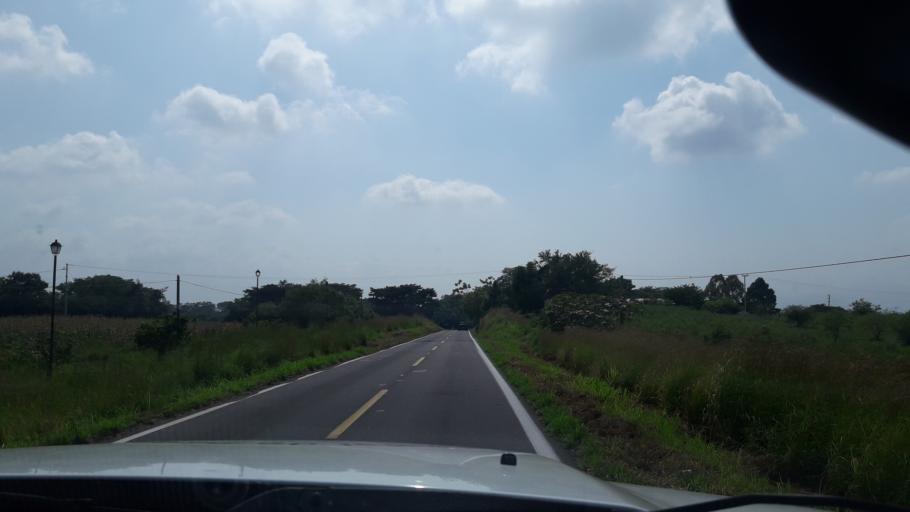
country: MX
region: Colima
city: Suchitlan
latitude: 19.3839
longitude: -103.7113
